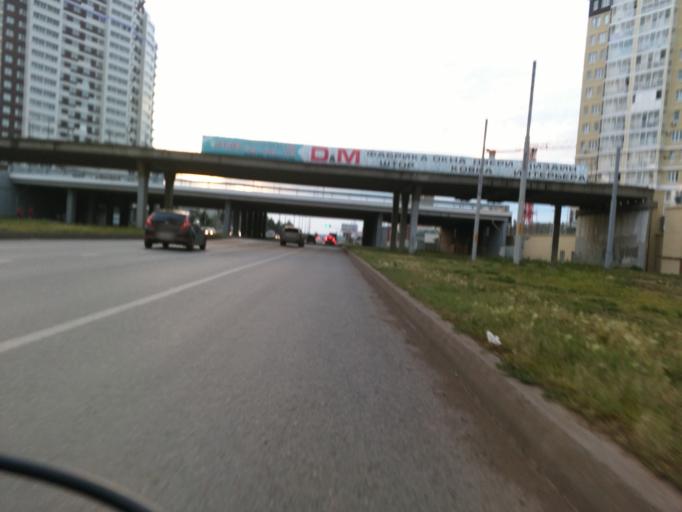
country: RU
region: Tatarstan
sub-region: Tukayevskiy Rayon
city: Naberezhnyye Chelny
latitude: 55.7516
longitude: 52.4138
